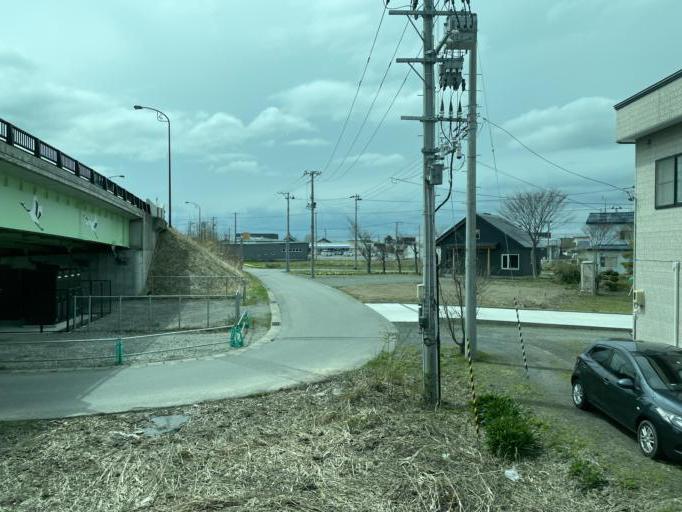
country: JP
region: Aomori
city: Goshogawara
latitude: 40.7638
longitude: 140.4352
